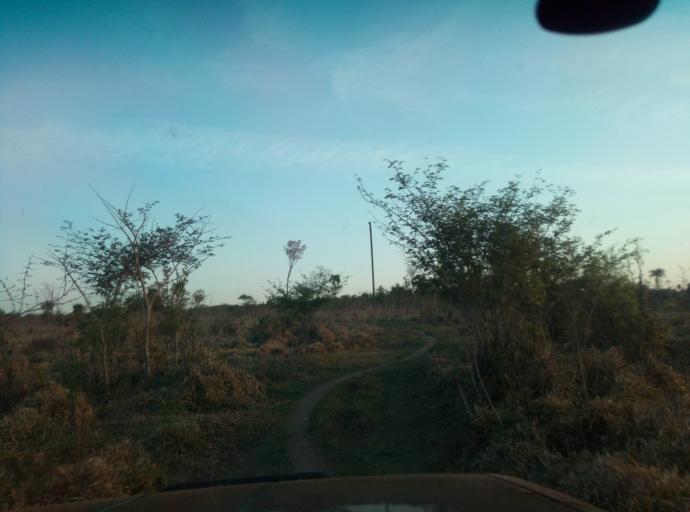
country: PY
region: Caaguazu
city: Yhu
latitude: -25.2010
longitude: -56.1081
